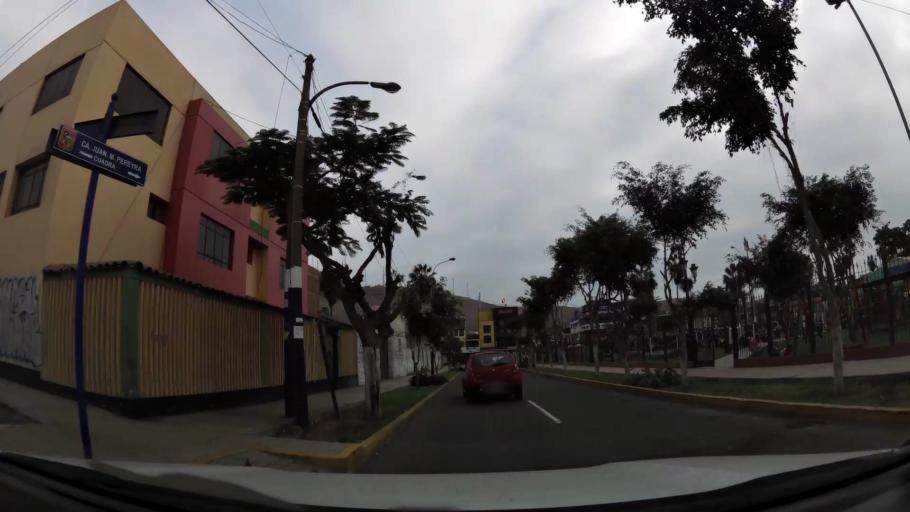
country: PE
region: Lima
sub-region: Lima
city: Surco
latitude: -12.1714
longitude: -77.0209
